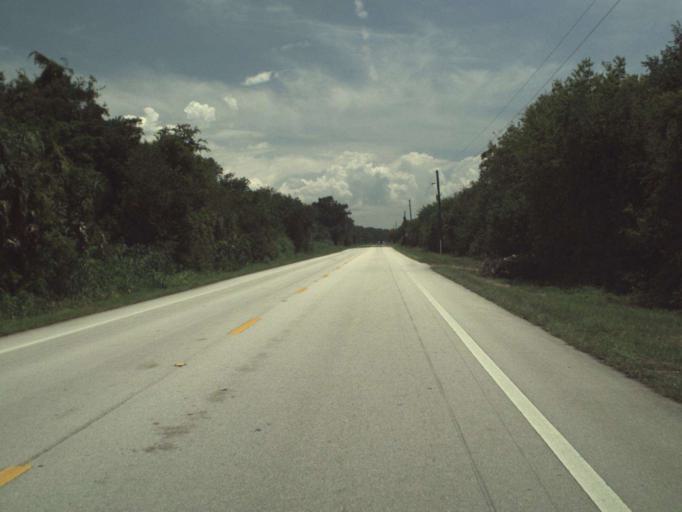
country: US
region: Florida
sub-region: Martin County
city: Indiantown
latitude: 27.0089
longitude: -80.6253
